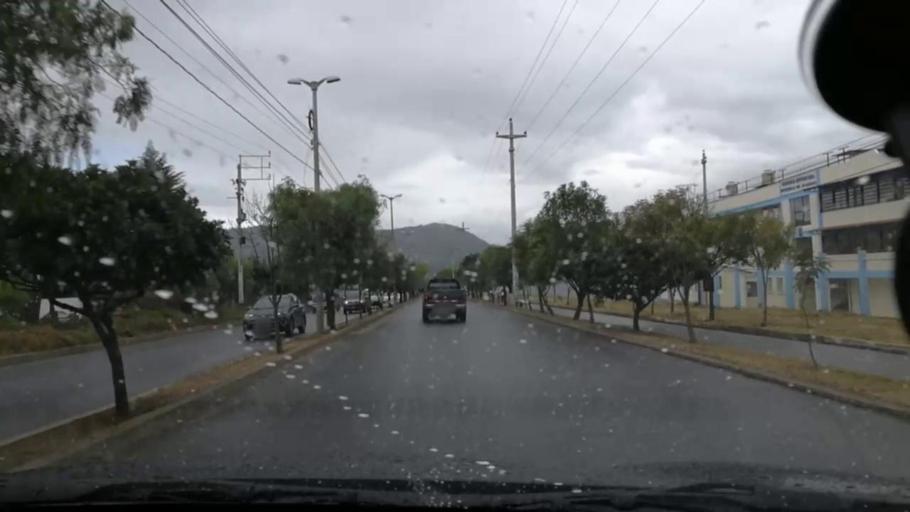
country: PE
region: Cajamarca
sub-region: Provincia de Cajamarca
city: Cajamarca
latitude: -7.1653
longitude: -78.4916
